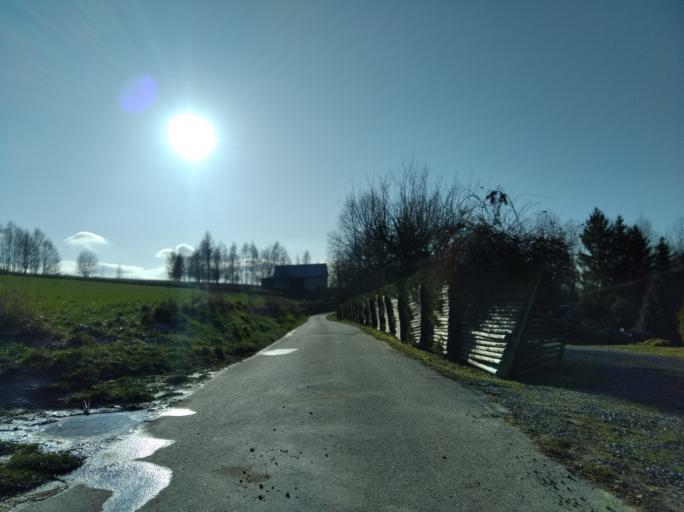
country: PL
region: Subcarpathian Voivodeship
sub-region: Powiat strzyzowski
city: Polomia
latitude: 49.8850
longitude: 21.8488
